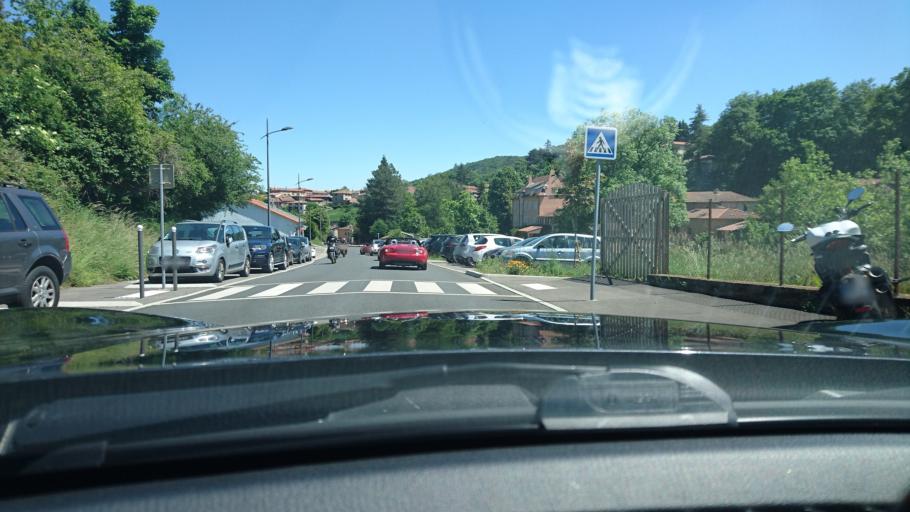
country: FR
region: Rhone-Alpes
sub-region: Departement du Rhone
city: Courzieu
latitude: 45.7084
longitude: 4.5856
